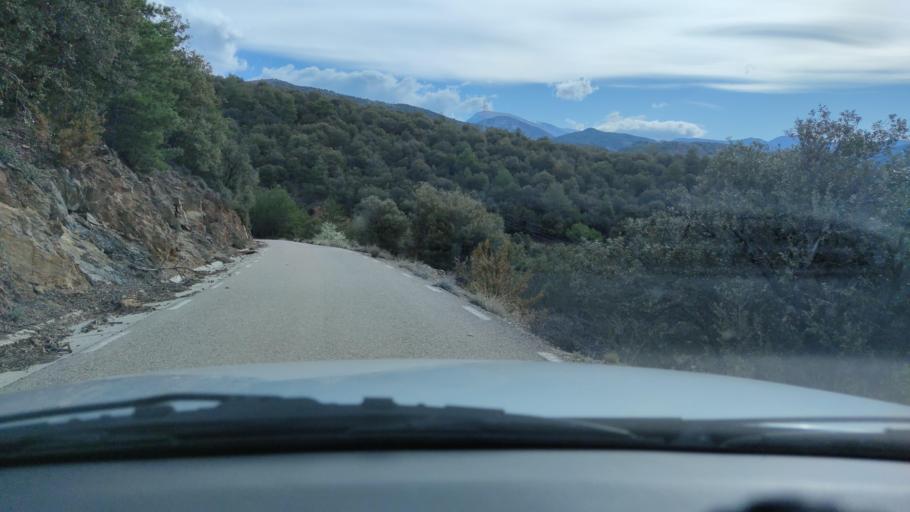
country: ES
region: Catalonia
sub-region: Provincia de Lleida
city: la Seu d'Urgell
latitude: 42.2416
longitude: 1.4261
